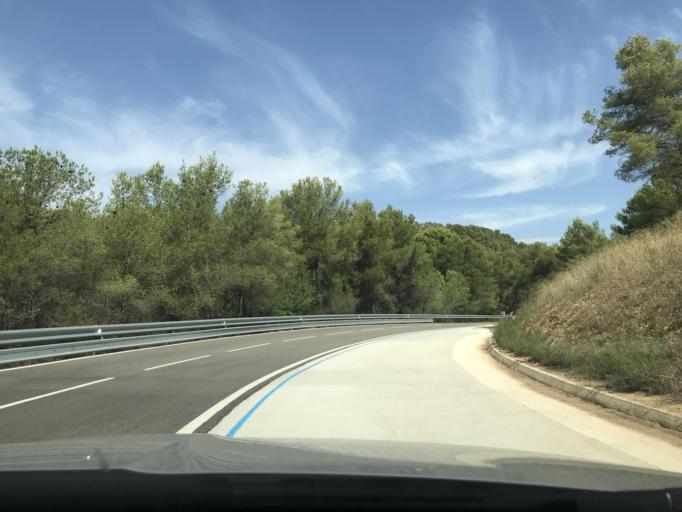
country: ES
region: Catalonia
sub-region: Provincia de Tarragona
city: Salomo
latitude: 41.1961
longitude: 1.3847
